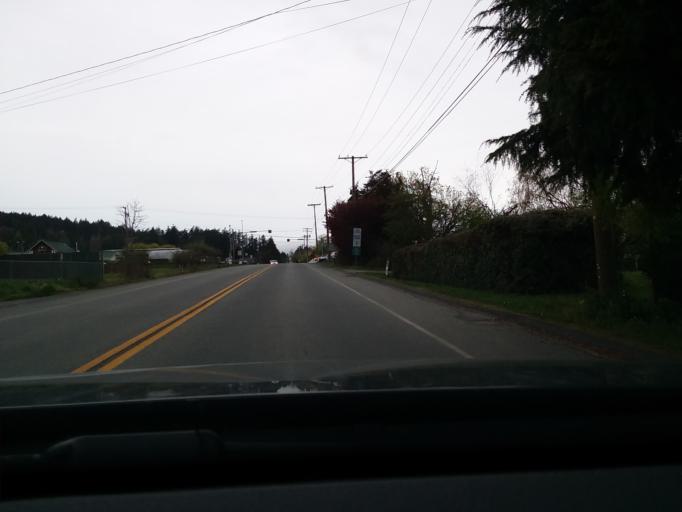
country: CA
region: British Columbia
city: North Saanich
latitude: 48.6300
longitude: -123.4185
